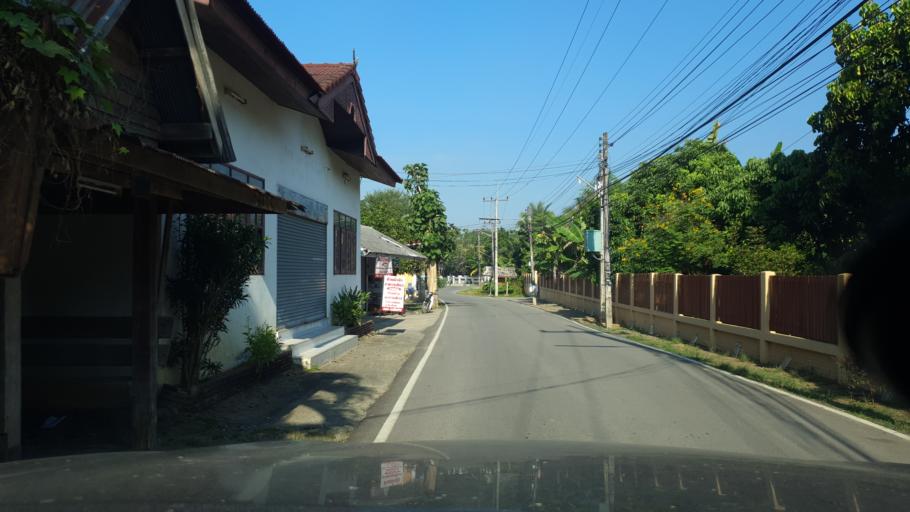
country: TH
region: Chiang Mai
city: San Kamphaeng
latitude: 18.7549
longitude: 99.1604
